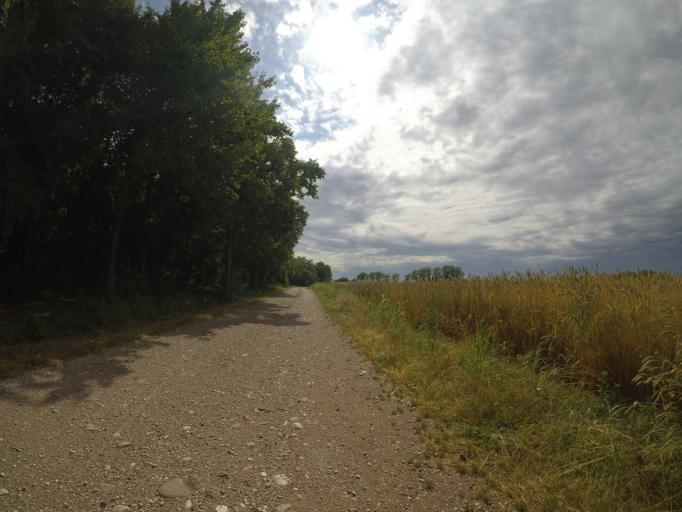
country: IT
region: Friuli Venezia Giulia
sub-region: Provincia di Udine
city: Lestizza
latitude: 45.9671
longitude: 13.1360
